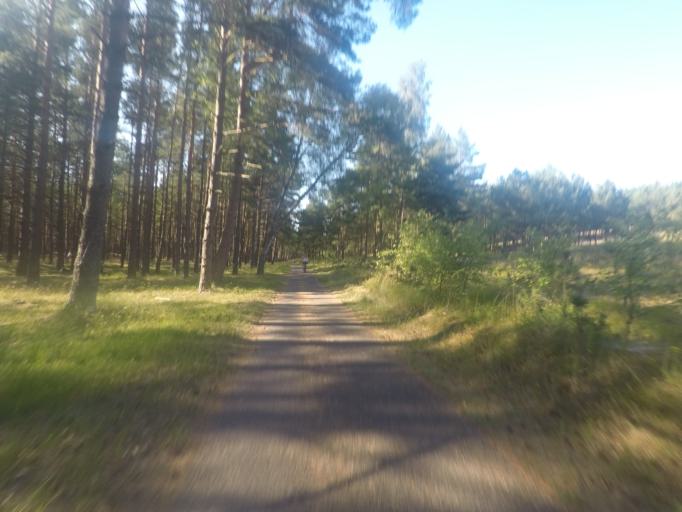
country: LT
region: Klaipedos apskritis
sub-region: Klaipeda
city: Klaipeda
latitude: 55.5788
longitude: 21.1143
